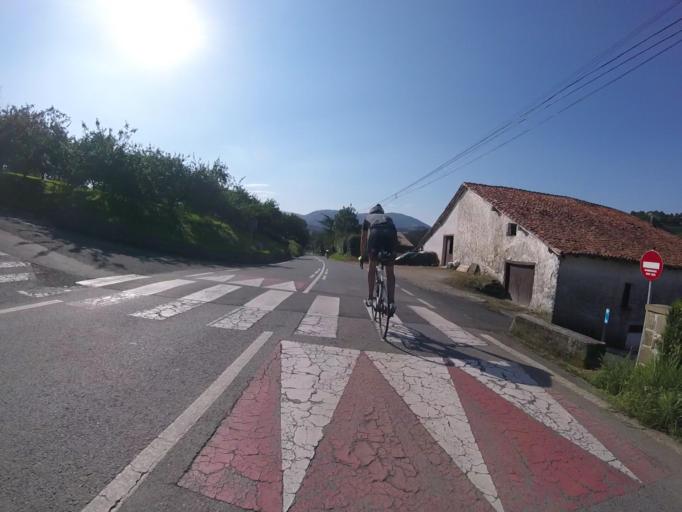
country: ES
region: Basque Country
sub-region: Provincia de Guipuzcoa
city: Asteasu
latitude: 43.1954
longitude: -2.0976
